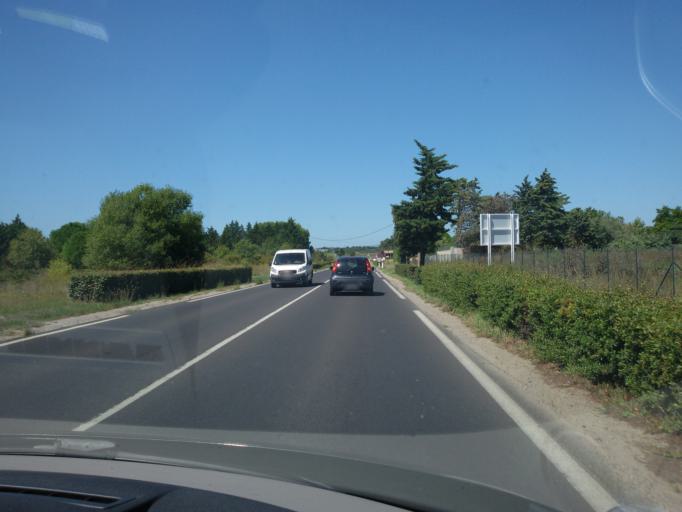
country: FR
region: Languedoc-Roussillon
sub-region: Departement de l'Herault
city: Villeneuve-les-Maguelone
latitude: 43.5398
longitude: 3.8528
